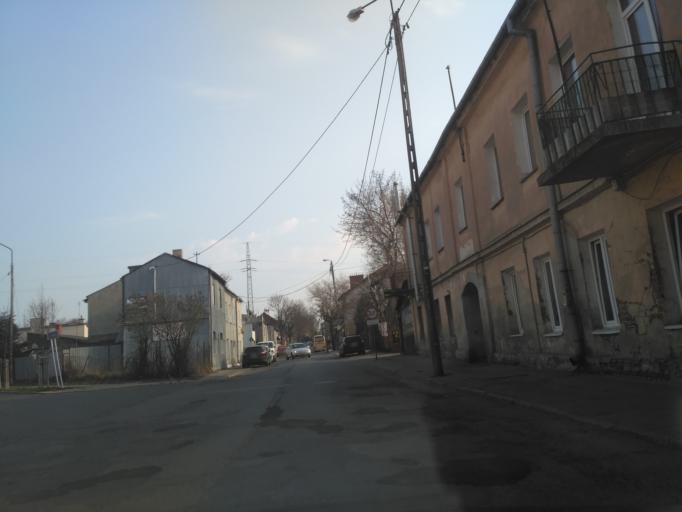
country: PL
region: Lublin Voivodeship
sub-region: Powiat lubelski
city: Lublin
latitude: 51.2320
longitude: 22.5784
